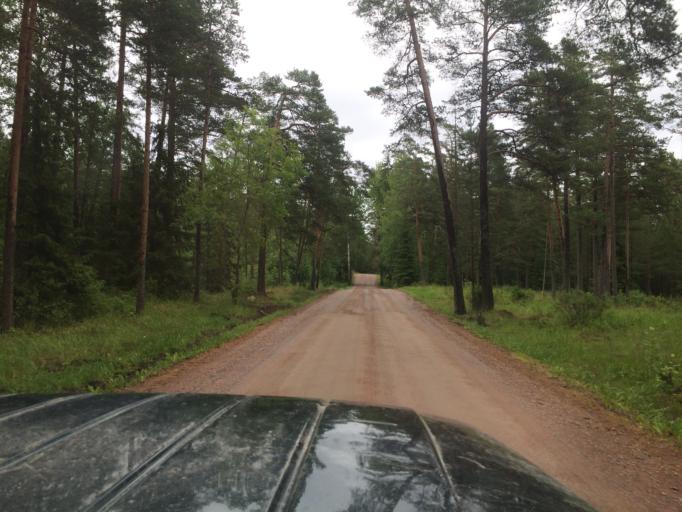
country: RU
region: Republic of Karelia
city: Sortavala
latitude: 61.3680
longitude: 30.9179
